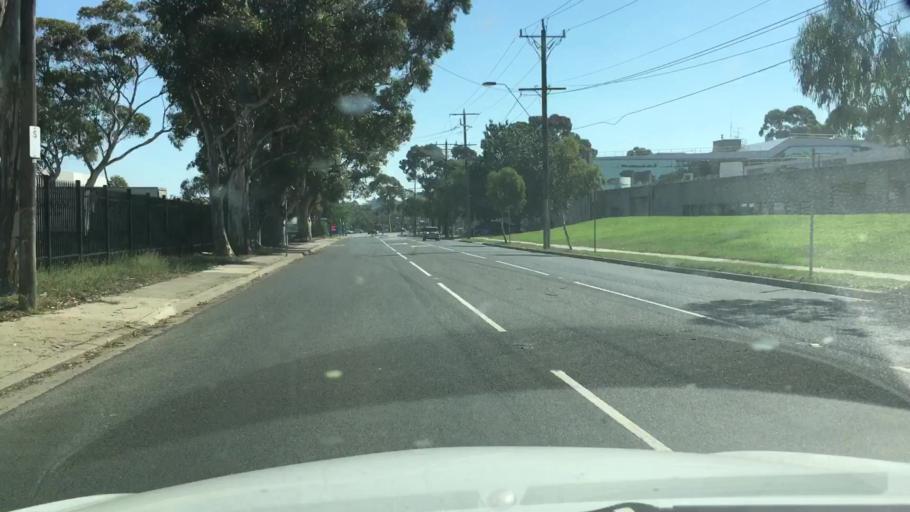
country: AU
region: Victoria
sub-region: Greater Dandenong
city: Noble Park North
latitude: -37.9519
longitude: 145.1819
